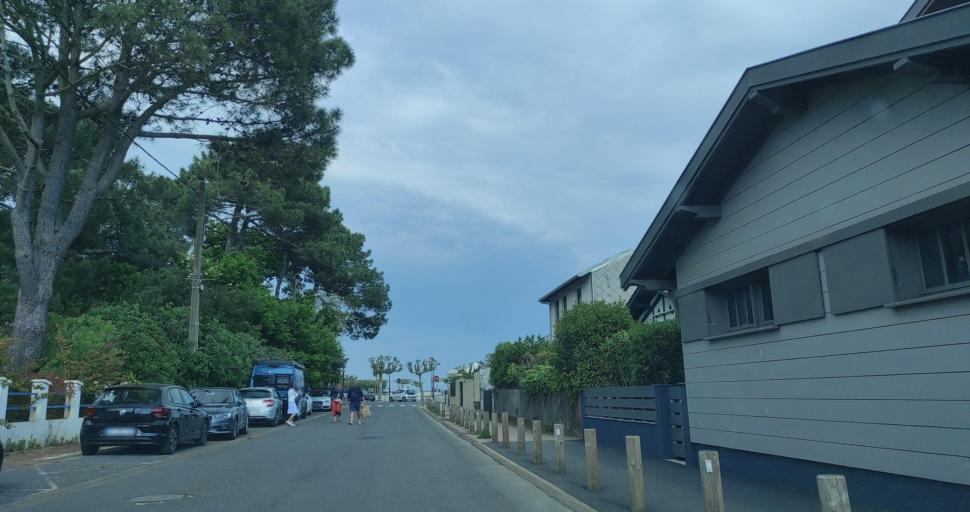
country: FR
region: Aquitaine
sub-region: Departement de la Gironde
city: Arcachon
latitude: 44.6518
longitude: -1.2441
